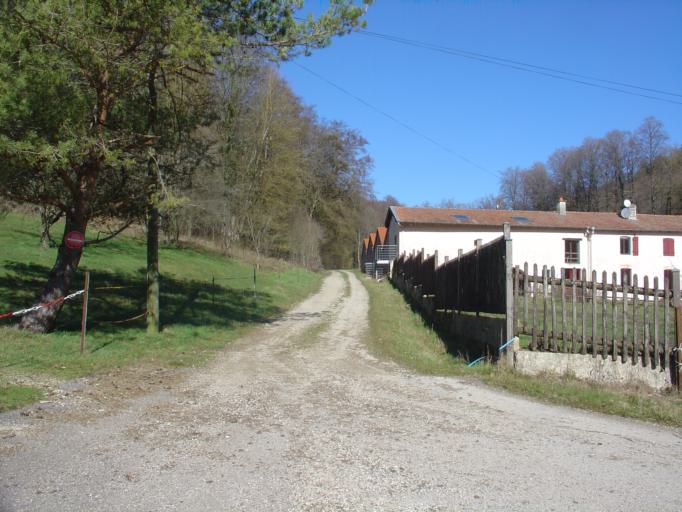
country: FR
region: Lorraine
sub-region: Departement de Meurthe-et-Moselle
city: Domgermain
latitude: 48.6135
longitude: 5.7980
